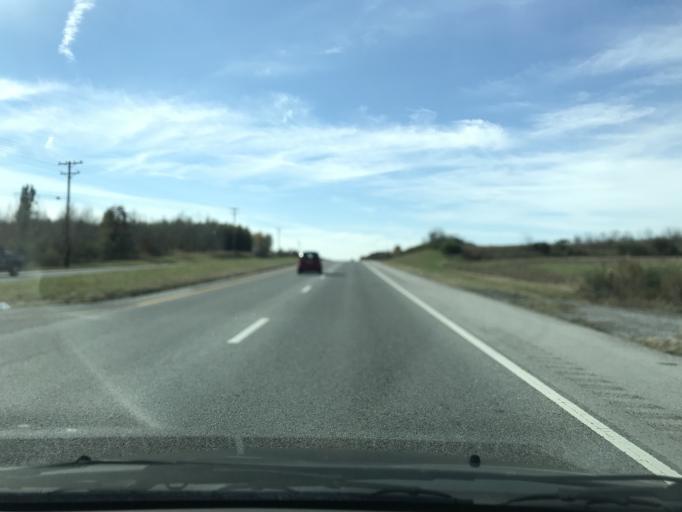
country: US
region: Tennessee
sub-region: Coffee County
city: Manchester
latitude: 35.4099
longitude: -86.1226
